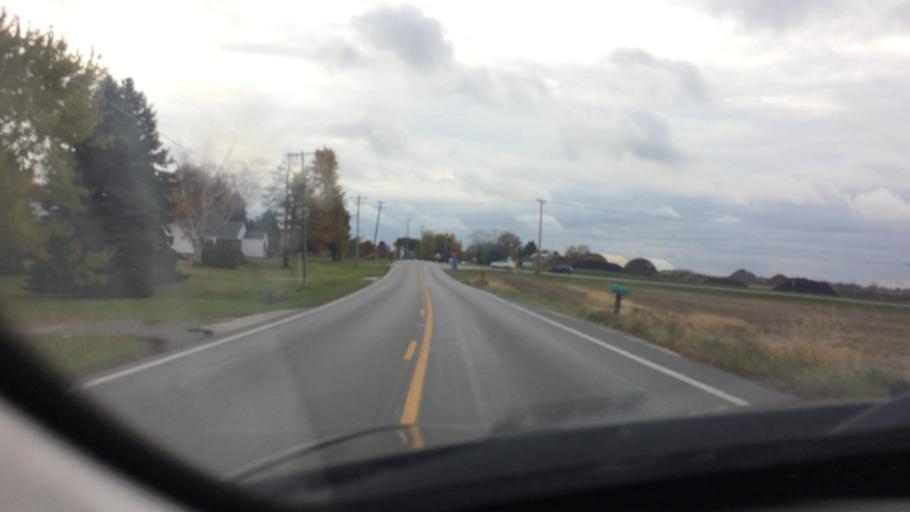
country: US
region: Ohio
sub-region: Hancock County
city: Findlay
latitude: 41.0408
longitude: -83.6868
